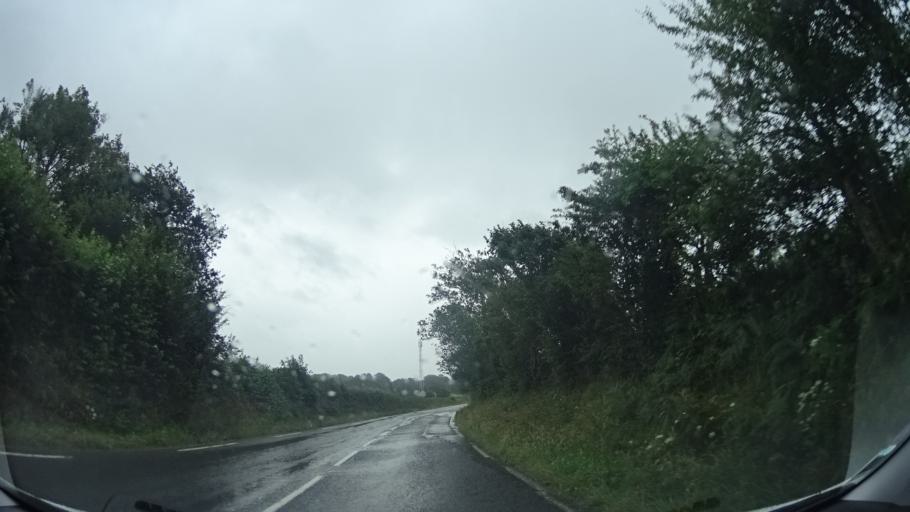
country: FR
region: Lower Normandy
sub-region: Departement de la Manche
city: Beaumont-Hague
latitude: 49.6055
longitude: -1.7857
